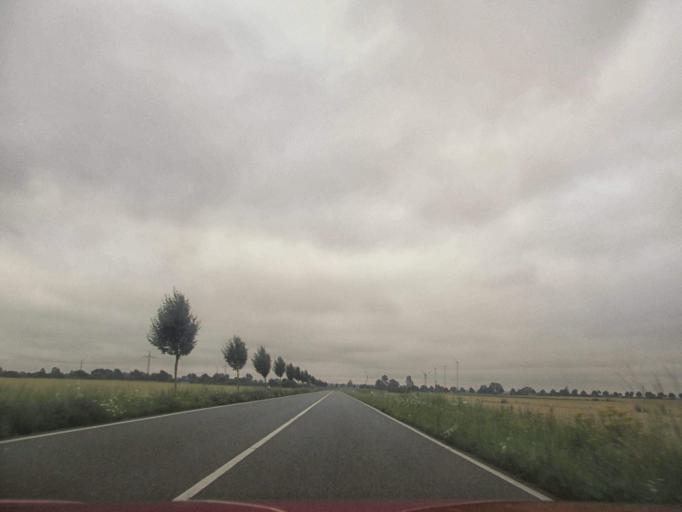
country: DE
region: Lower Saxony
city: Calberlah
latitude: 52.4117
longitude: 10.6716
